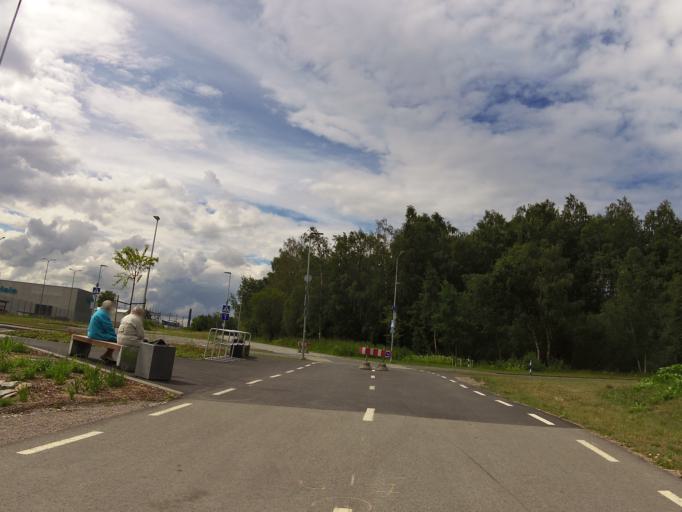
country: EE
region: Harju
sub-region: Tallinna linn
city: Tallinn
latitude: 59.4195
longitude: 24.6738
